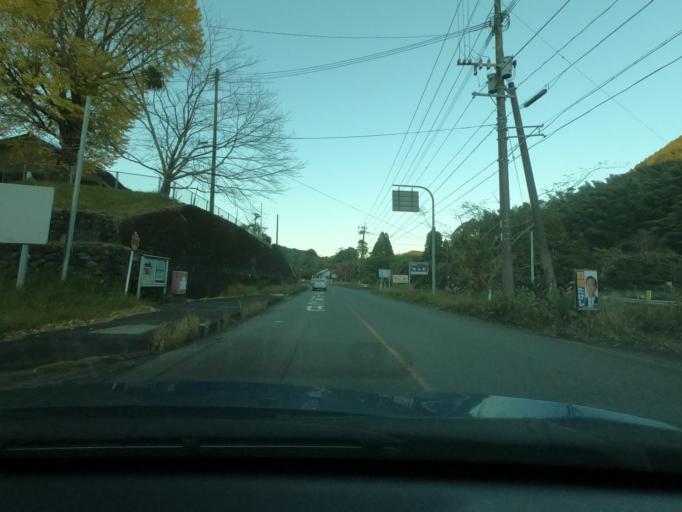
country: JP
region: Kagoshima
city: Satsumasendai
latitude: 31.8053
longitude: 130.4818
